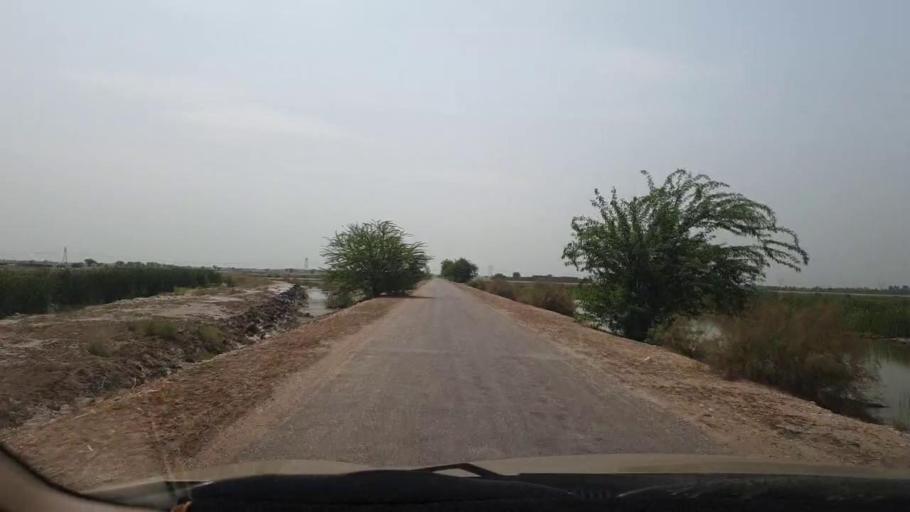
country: PK
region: Sindh
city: Goth Garelo
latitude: 27.5001
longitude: 68.1159
